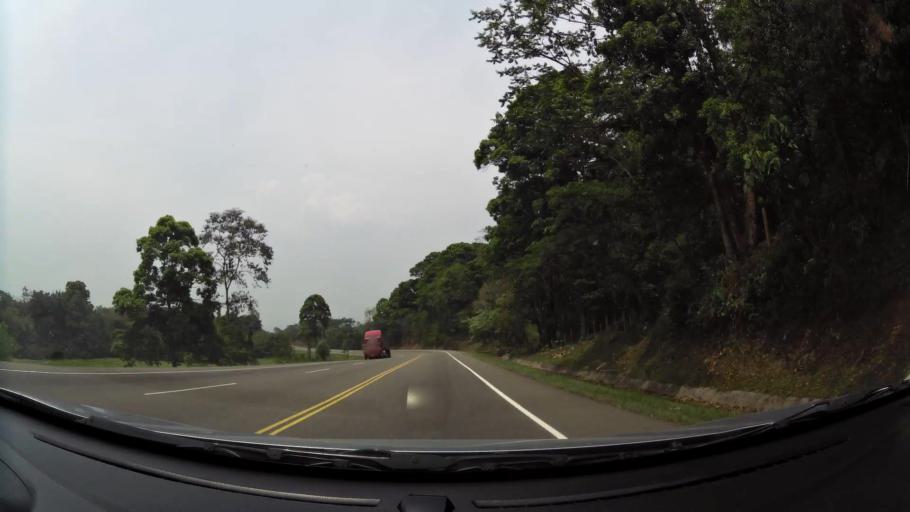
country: HN
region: Cortes
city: Santa Cruz de Yojoa
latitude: 14.9721
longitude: -87.9340
